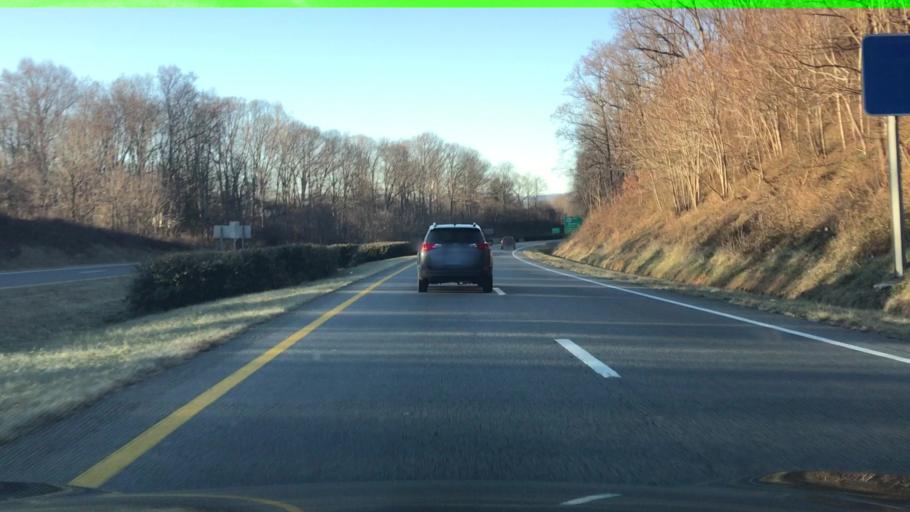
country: US
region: Virginia
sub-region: City of Bedford
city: Bedford
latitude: 37.3266
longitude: -79.5388
